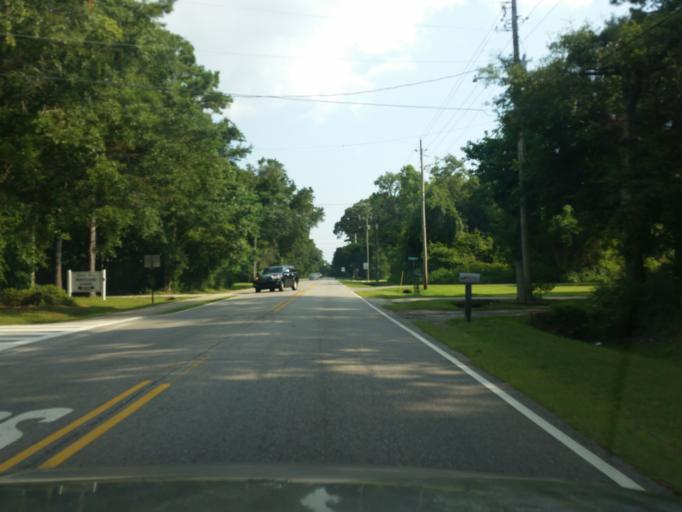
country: US
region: Alabama
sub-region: Baldwin County
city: Daphne
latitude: 30.5912
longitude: -87.9028
